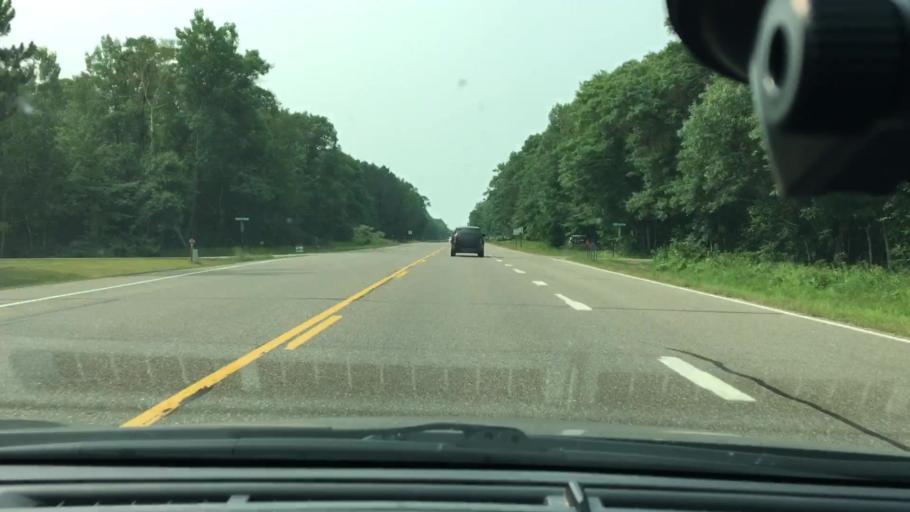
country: US
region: Minnesota
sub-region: Crow Wing County
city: Breezy Point
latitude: 46.5125
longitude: -94.1333
